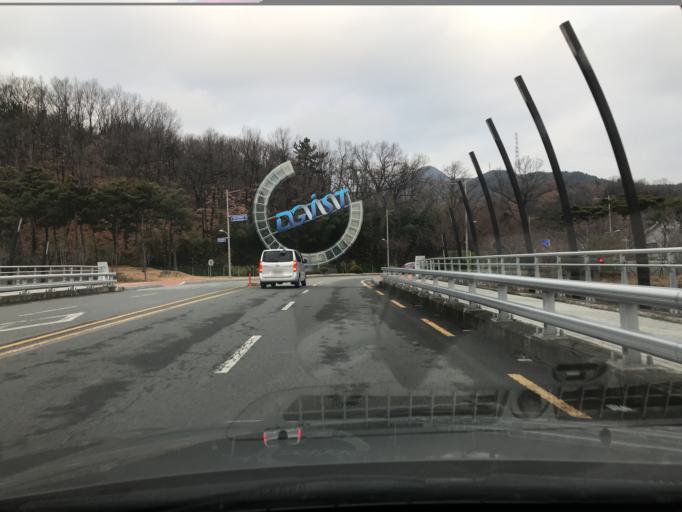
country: KR
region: Daegu
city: Hwawon
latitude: 35.6997
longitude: 128.4578
